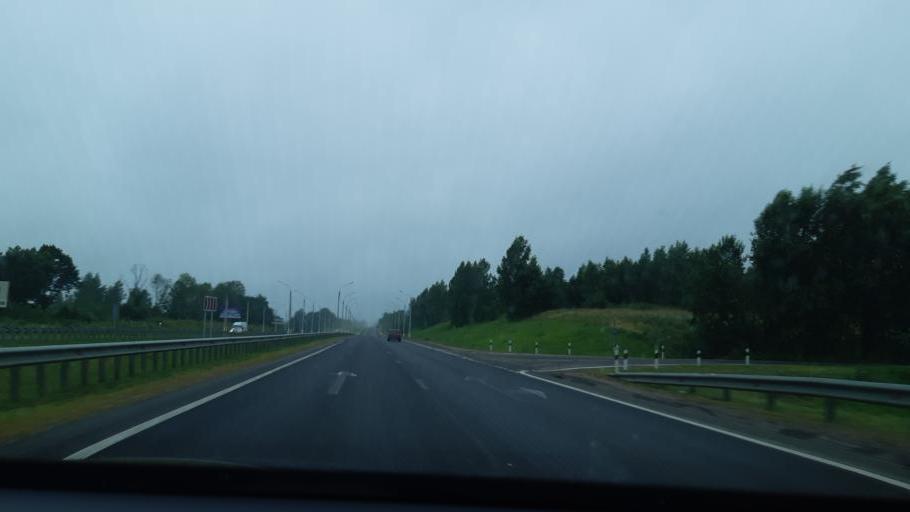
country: RU
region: Smolensk
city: Talashkino
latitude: 54.5848
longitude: 32.2272
